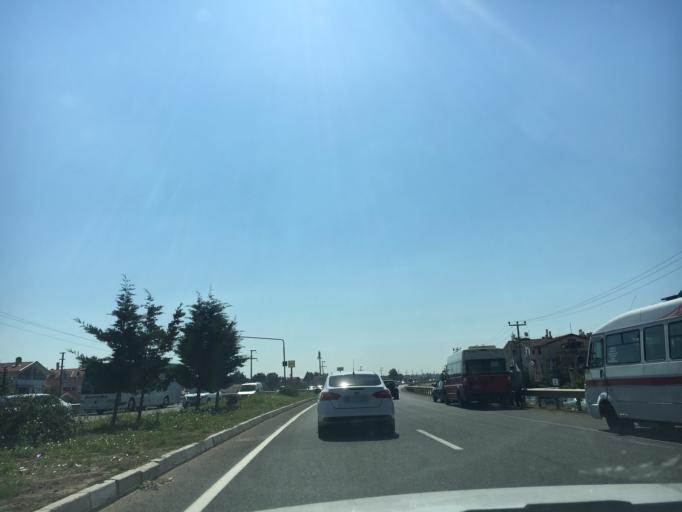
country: TR
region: Tekirdag
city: Marmara Ereglisi
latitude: 40.9936
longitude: 27.8424
